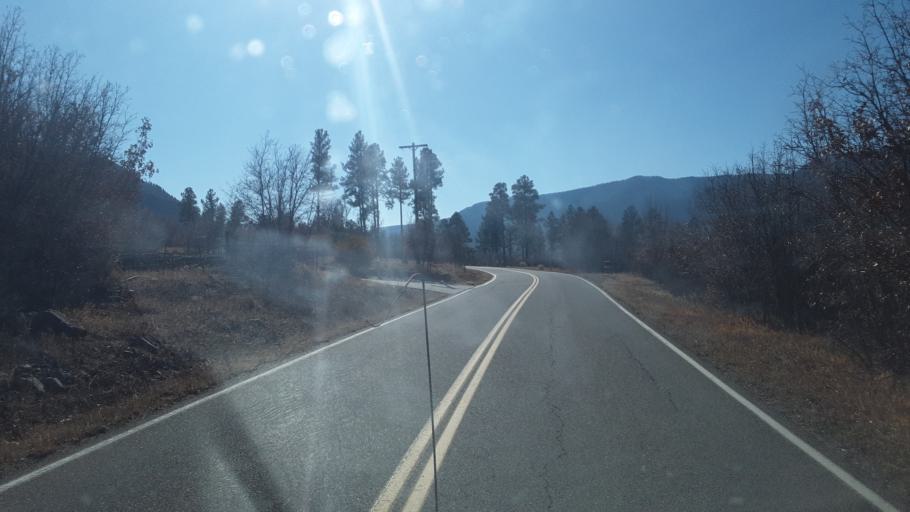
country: US
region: Colorado
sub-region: La Plata County
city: Durango
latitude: 37.4124
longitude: -107.8105
